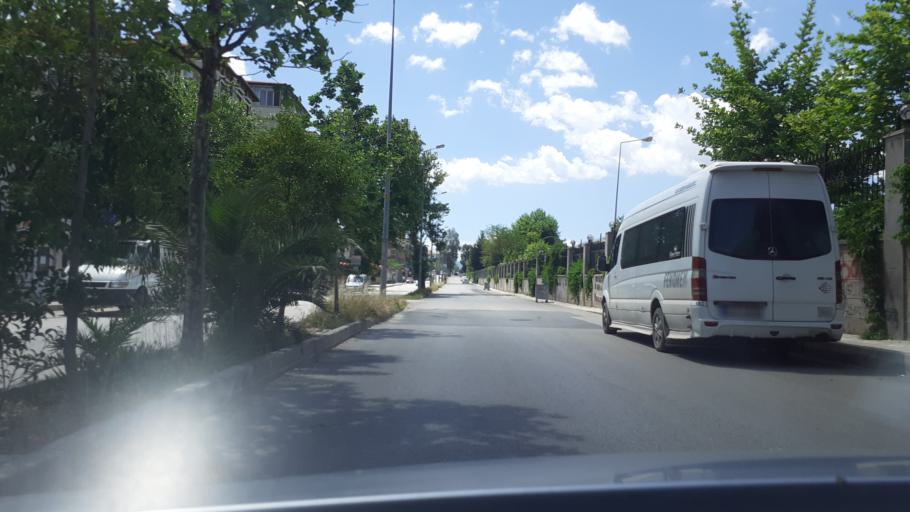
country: TR
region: Hatay
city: Anayazi
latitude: 36.3322
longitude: 36.1995
